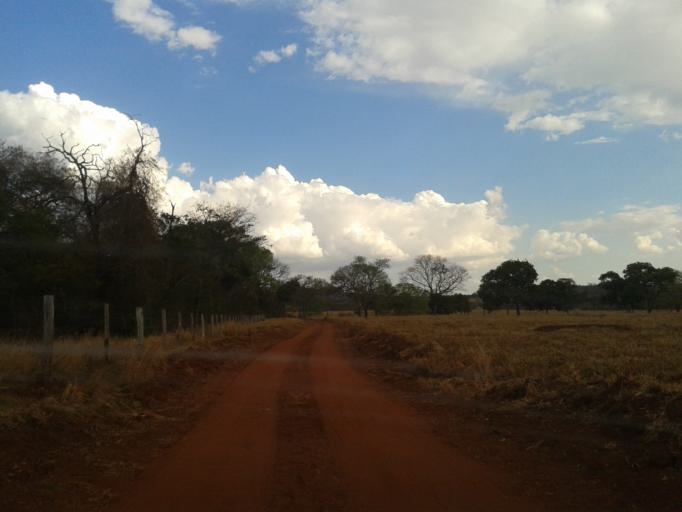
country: BR
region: Minas Gerais
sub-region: Santa Vitoria
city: Santa Vitoria
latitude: -19.1778
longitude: -49.9455
